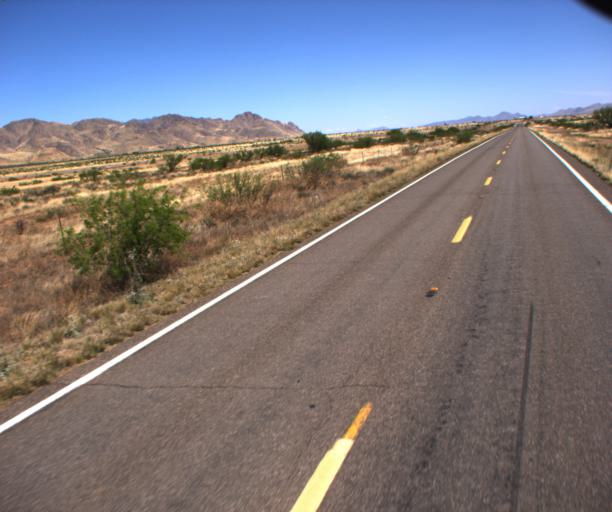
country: US
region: Arizona
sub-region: Cochise County
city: Douglas
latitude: 31.6780
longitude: -109.1415
